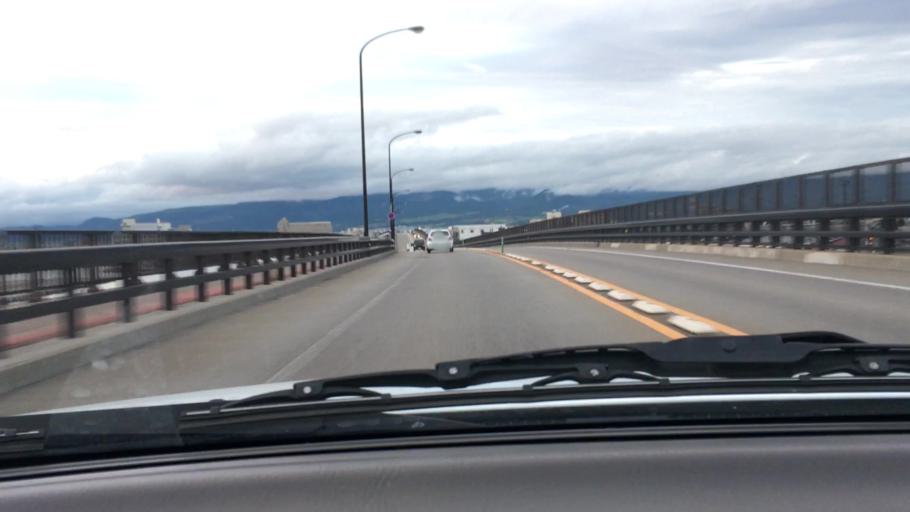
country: JP
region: Hokkaido
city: Hakodate
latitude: 41.7762
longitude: 140.7254
